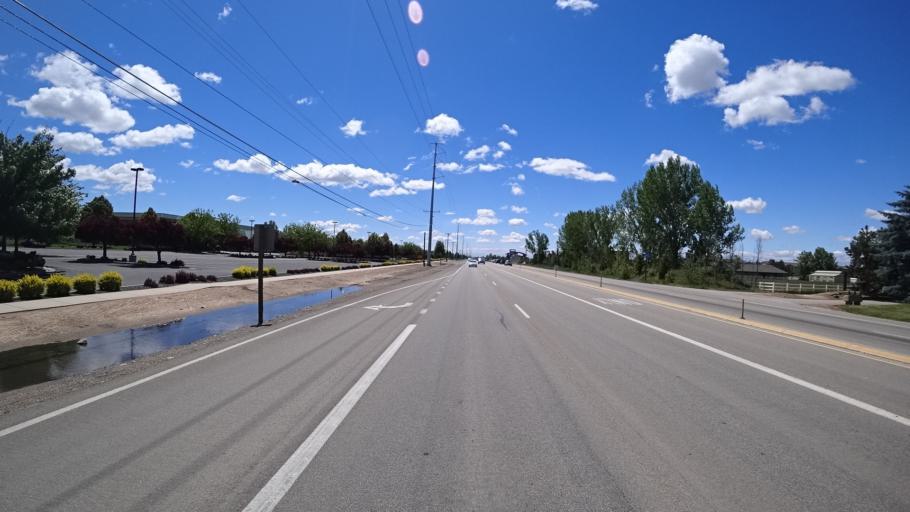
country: US
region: Idaho
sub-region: Ada County
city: Meridian
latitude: 43.6408
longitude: -116.3542
